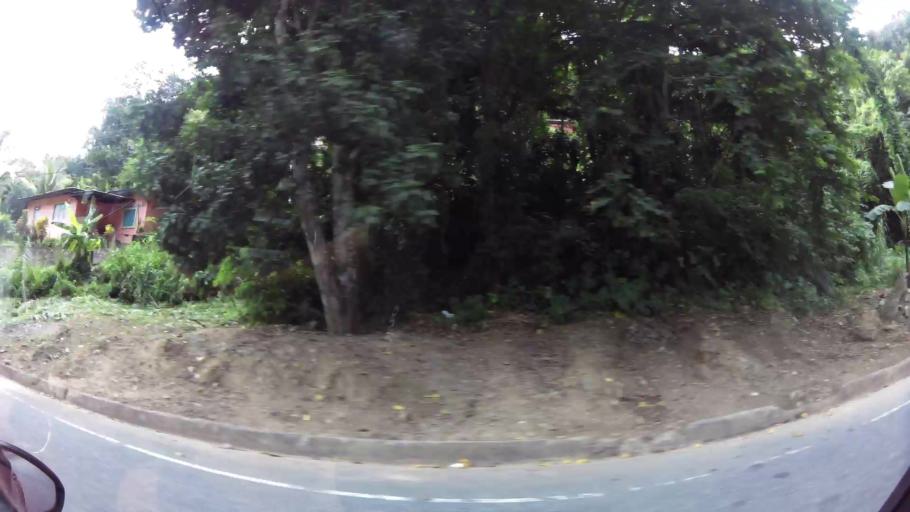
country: TT
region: Diego Martin
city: Petit Valley
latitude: 10.7136
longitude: -61.5174
